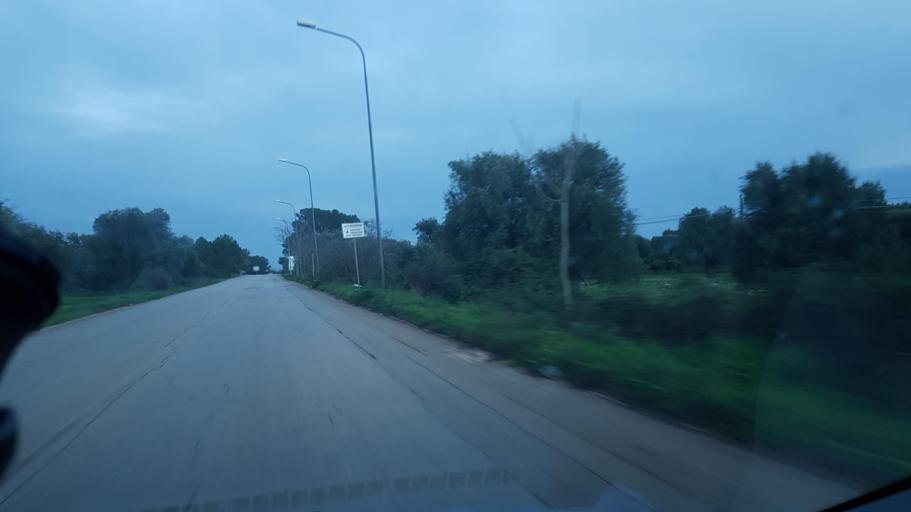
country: IT
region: Apulia
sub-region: Provincia di Brindisi
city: Ceglie Messapica
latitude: 40.6448
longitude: 17.5306
